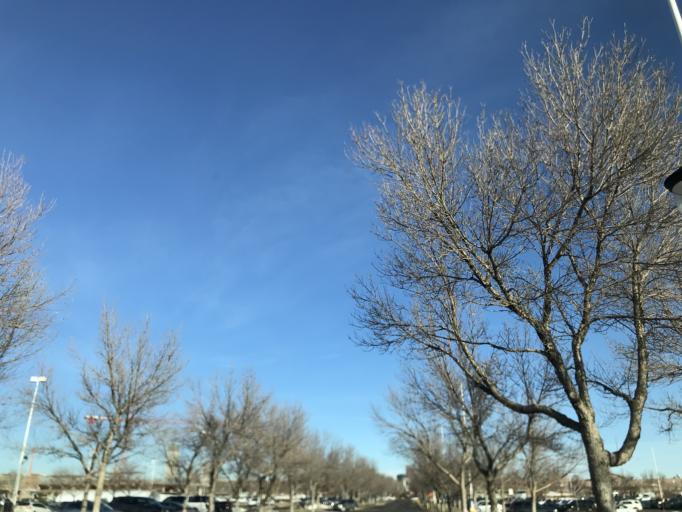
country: US
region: Colorado
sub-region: Denver County
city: Denver
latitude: 39.7077
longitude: -104.9900
